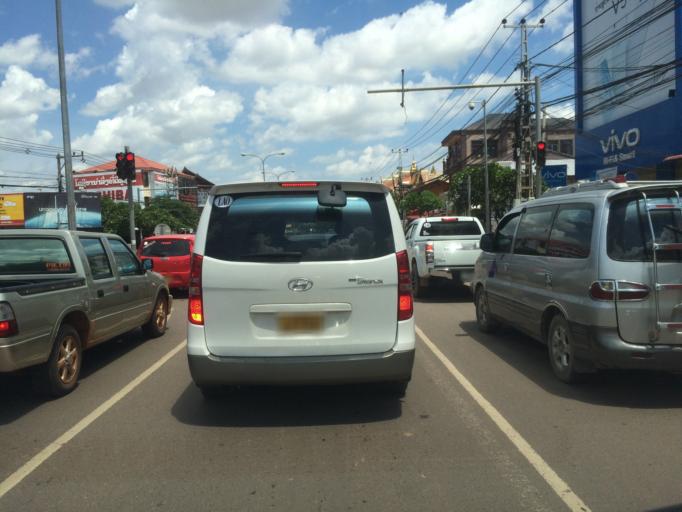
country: TH
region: Nong Khai
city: Si Chiang Mai
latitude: 17.9702
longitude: 102.5717
